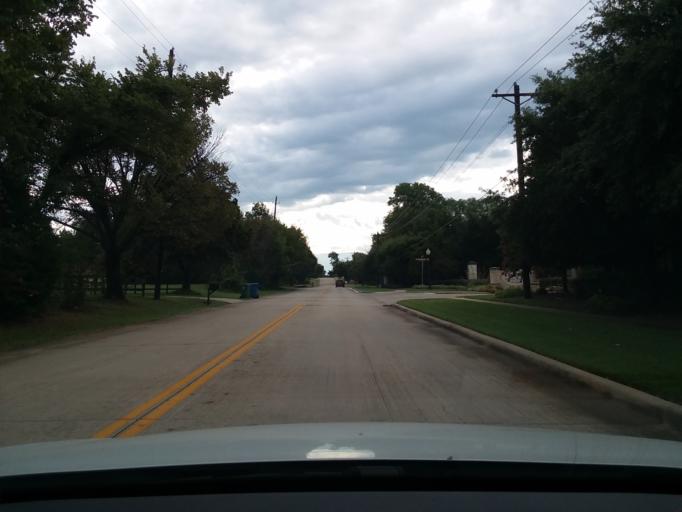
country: US
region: Texas
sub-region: Denton County
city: Highland Village
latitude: 33.0591
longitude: -97.0689
